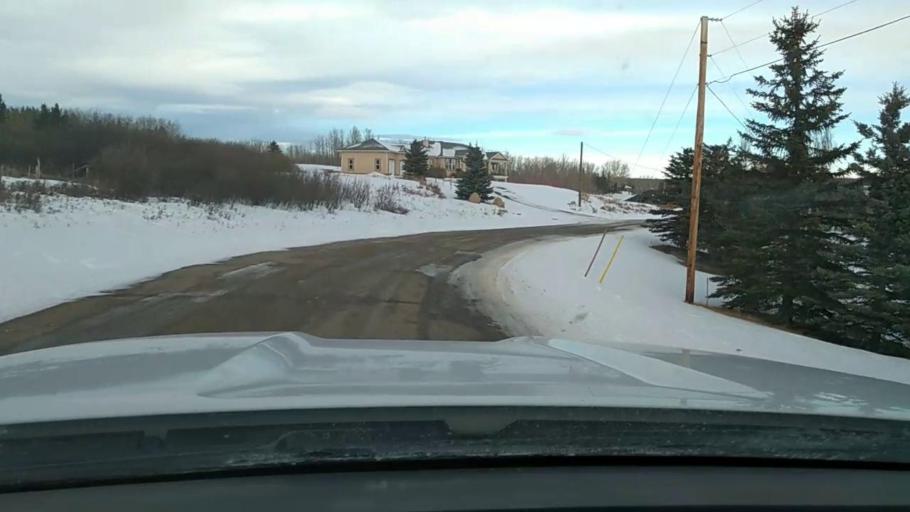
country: CA
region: Alberta
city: Cochrane
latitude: 51.1513
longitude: -114.2694
